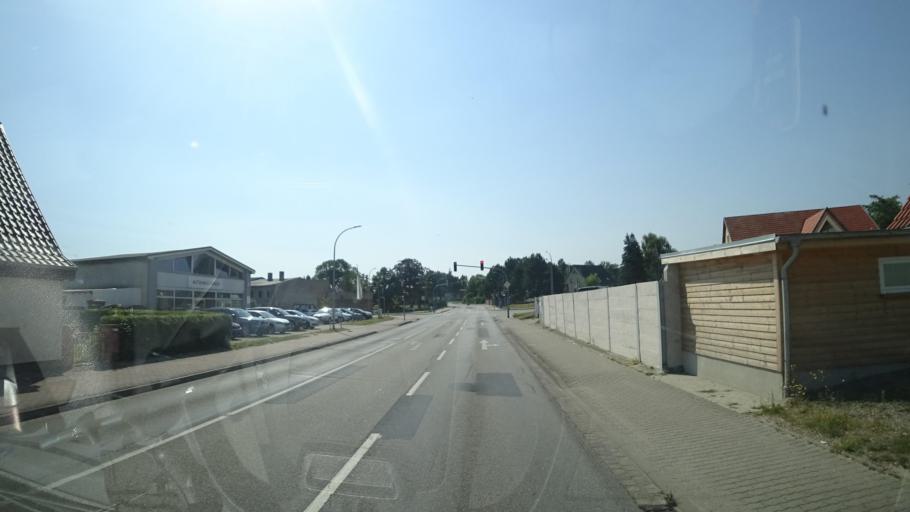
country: DE
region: Mecklenburg-Vorpommern
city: Wolgast
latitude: 54.0569
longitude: 13.7675
